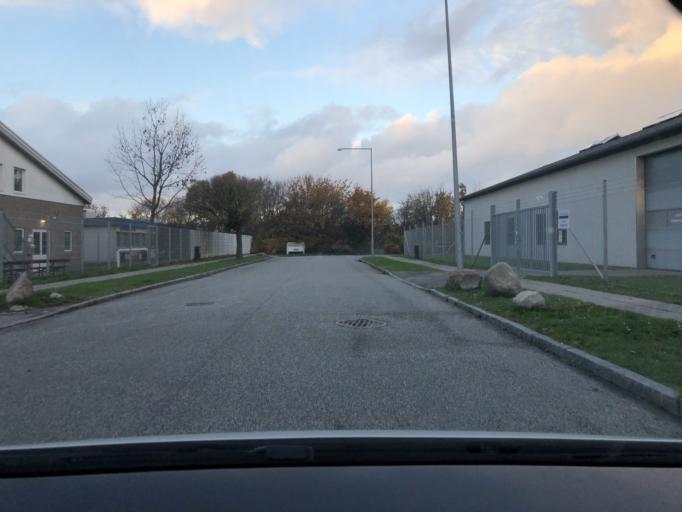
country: DK
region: Capital Region
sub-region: Tarnby Kommune
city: Tarnby
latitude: 55.6174
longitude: 12.6220
